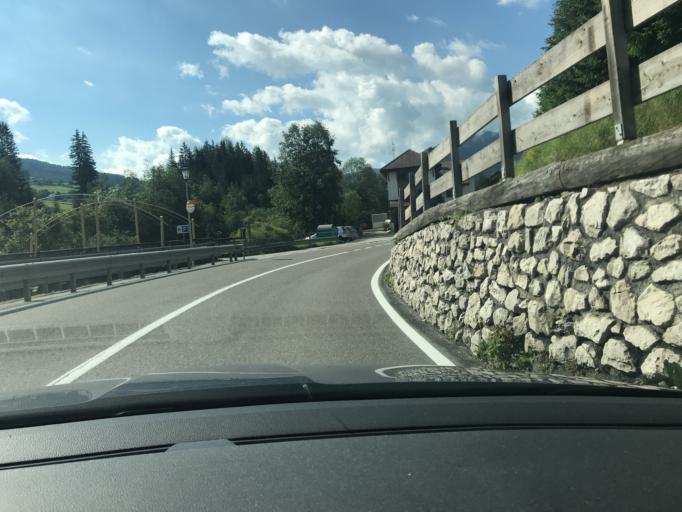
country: IT
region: Trentino-Alto Adige
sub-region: Bolzano
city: Badia
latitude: 46.6074
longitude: 11.8958
